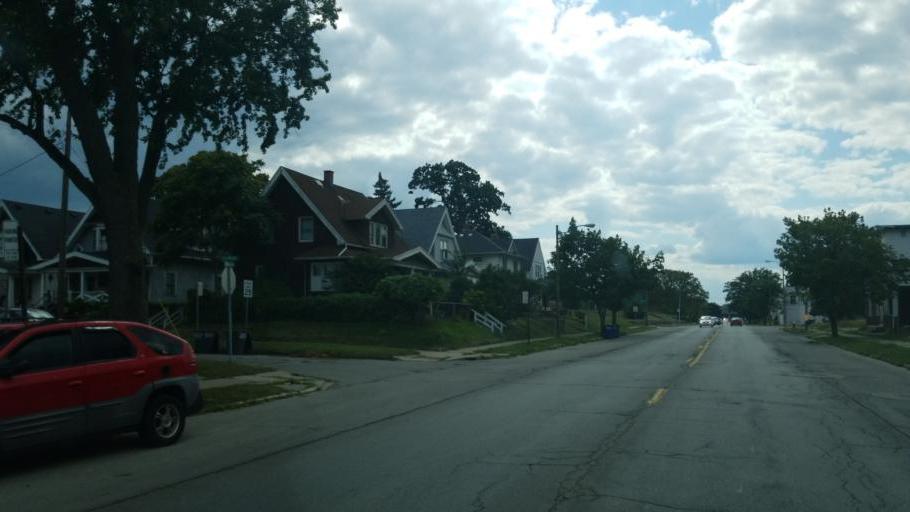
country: US
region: Ohio
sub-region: Wood County
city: Rossford
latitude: 41.6264
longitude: -83.5637
